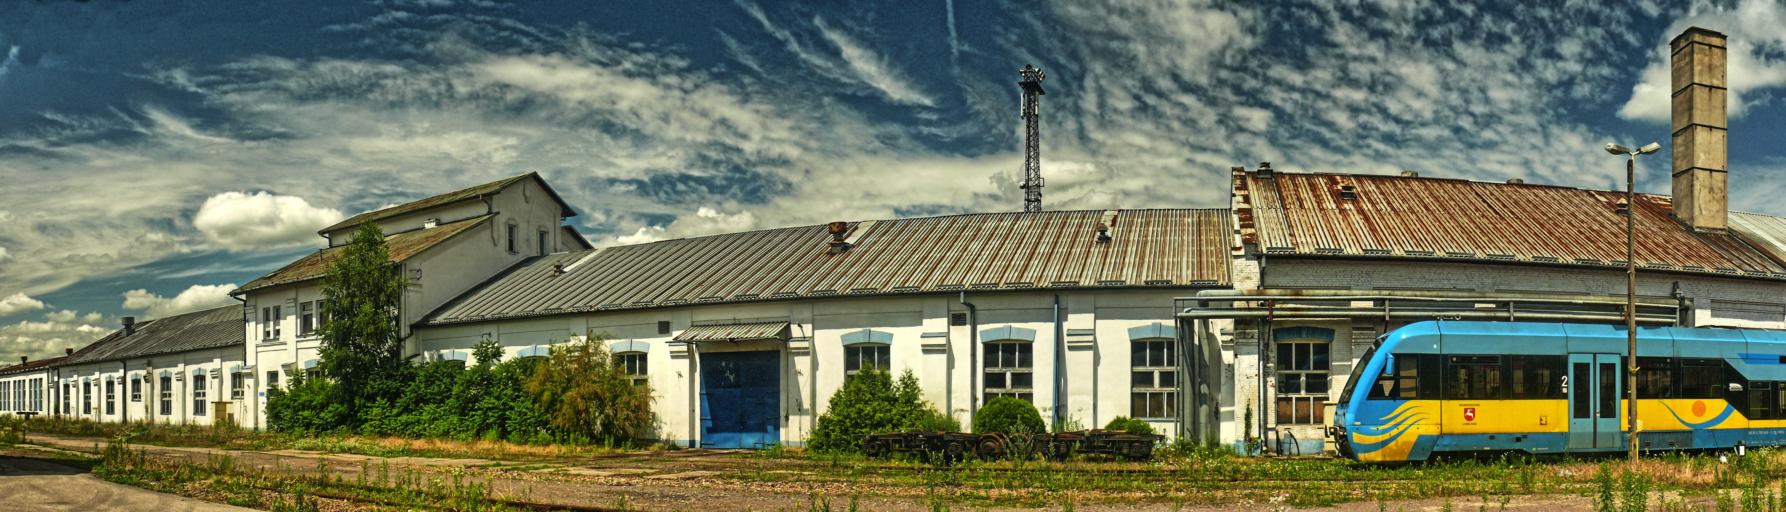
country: PL
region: Lublin Voivodeship
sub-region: Powiat lubelski
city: Lublin
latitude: 51.2285
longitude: 22.5642
